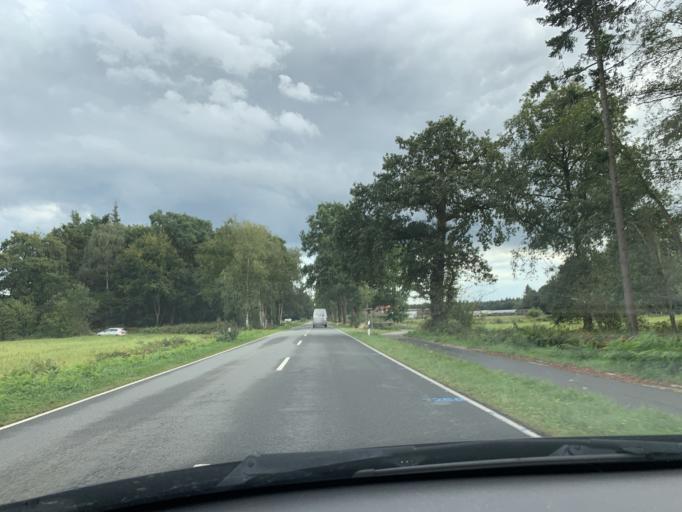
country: DE
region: Lower Saxony
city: Westerstede
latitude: 53.2991
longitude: 7.9171
